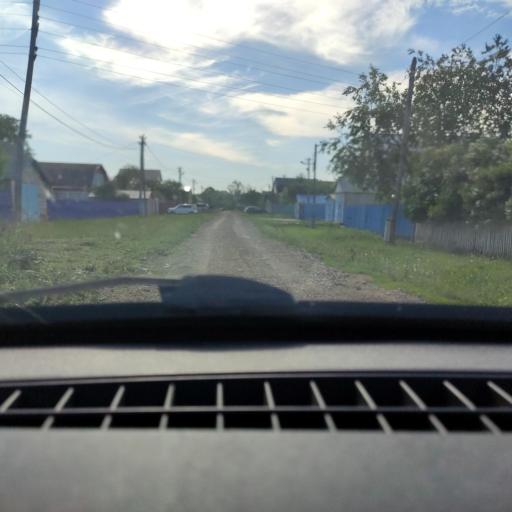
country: RU
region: Bashkortostan
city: Mikhaylovka
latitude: 54.7794
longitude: 55.8216
